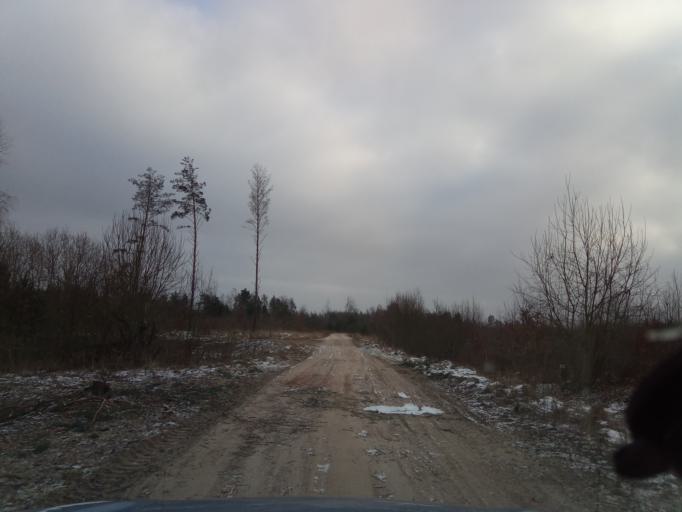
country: LT
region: Alytaus apskritis
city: Varena
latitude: 54.3702
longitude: 24.5399
